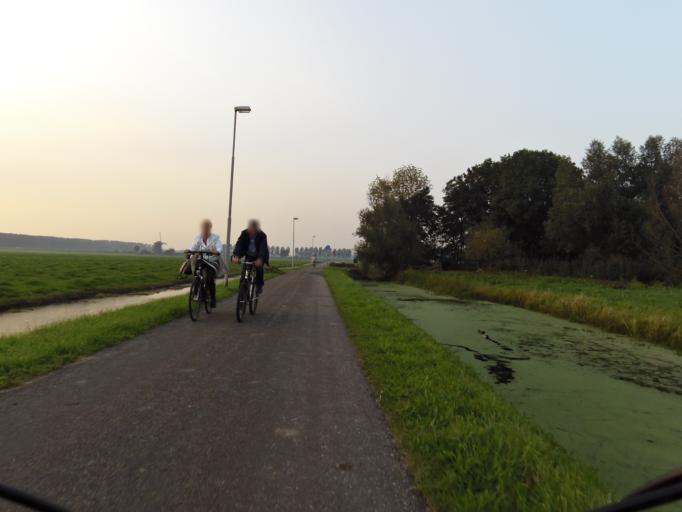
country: NL
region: South Holland
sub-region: Gemeente Voorschoten
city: Voorschoten
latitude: 52.1192
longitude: 4.4869
